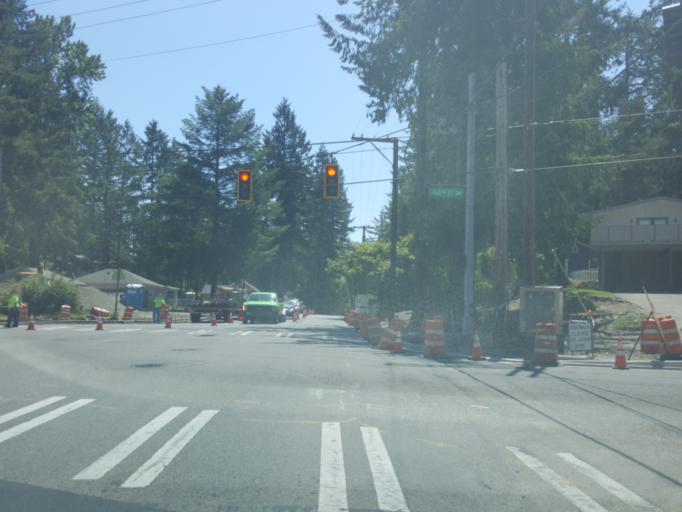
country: US
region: Washington
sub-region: Pierce County
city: Steilacoom
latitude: 47.1562
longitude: -122.5749
